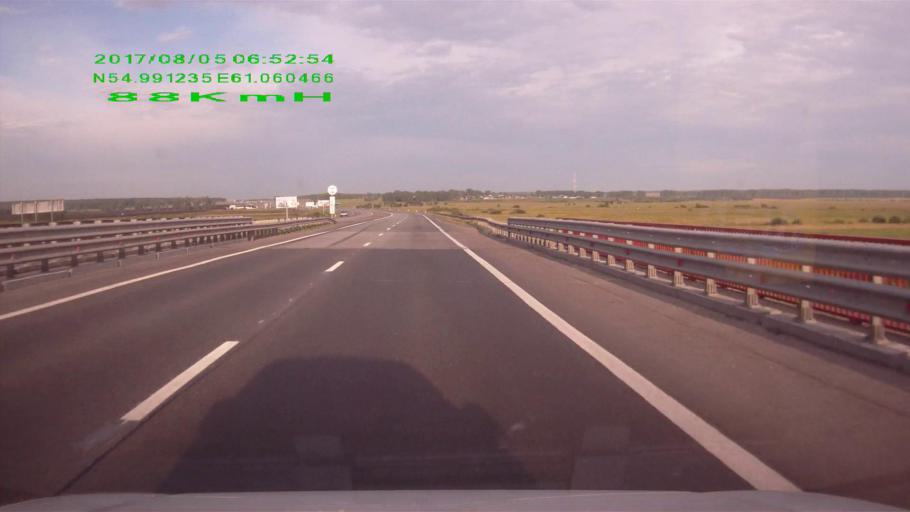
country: RU
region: Chelyabinsk
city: Poletayevo
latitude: 54.9912
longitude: 61.0593
